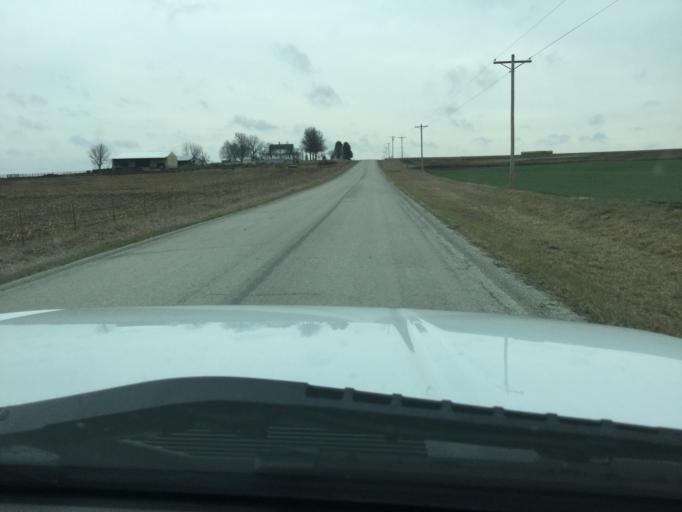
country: US
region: Kansas
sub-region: Nemaha County
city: Sabetha
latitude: 39.8615
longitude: -95.7142
